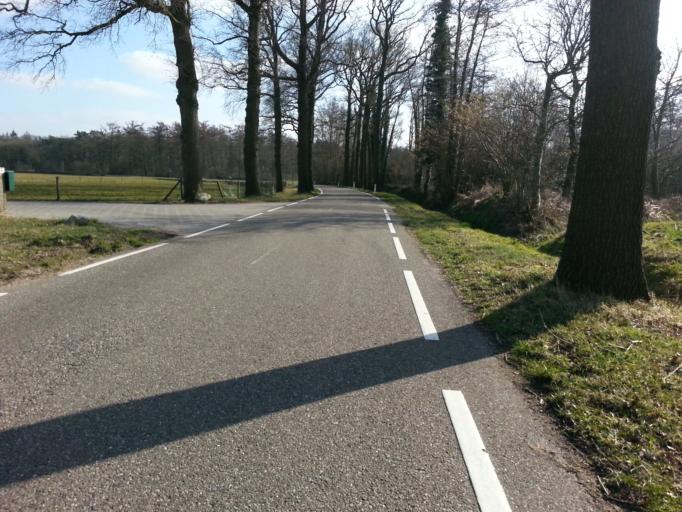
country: NL
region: Utrecht
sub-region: Gemeente Leusden
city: Leusden
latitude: 52.0947
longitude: 5.4754
